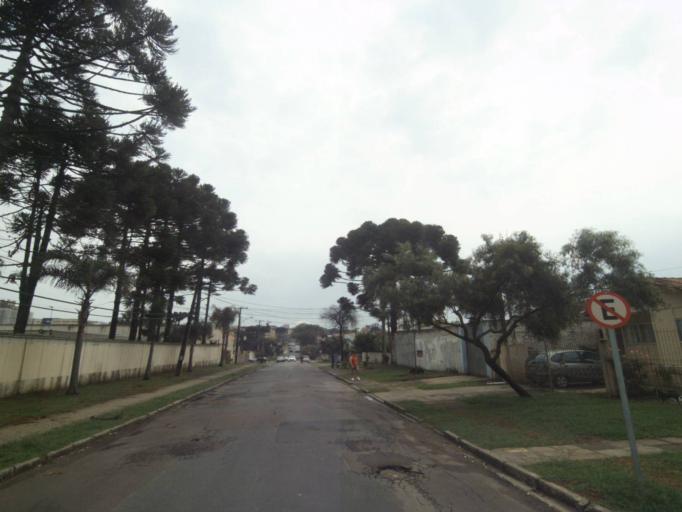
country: BR
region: Parana
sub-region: Curitiba
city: Curitiba
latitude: -25.4806
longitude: -49.2999
